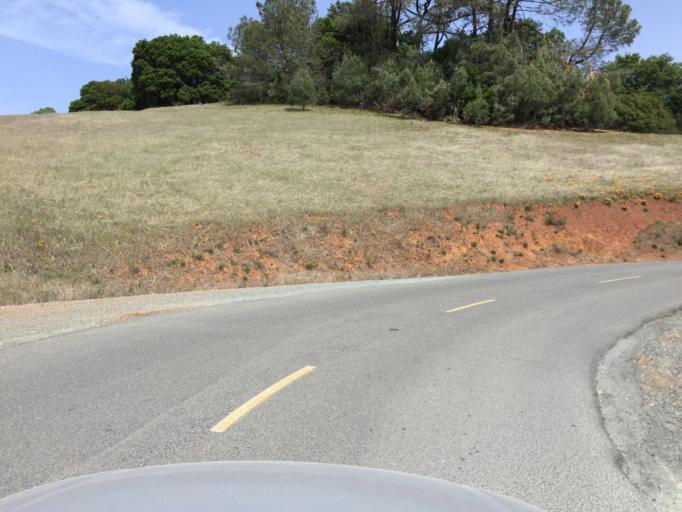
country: US
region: California
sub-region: Contra Costa County
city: Diablo
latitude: 37.8635
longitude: -121.9274
